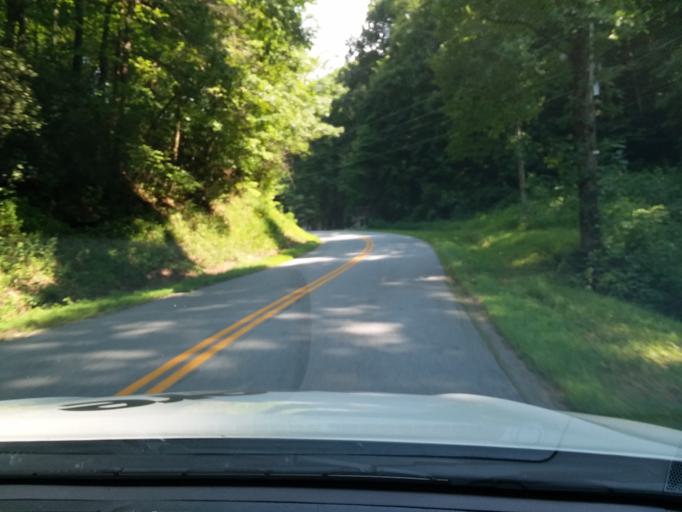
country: US
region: Georgia
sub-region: Rabun County
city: Clayton
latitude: 34.8645
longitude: -83.4715
